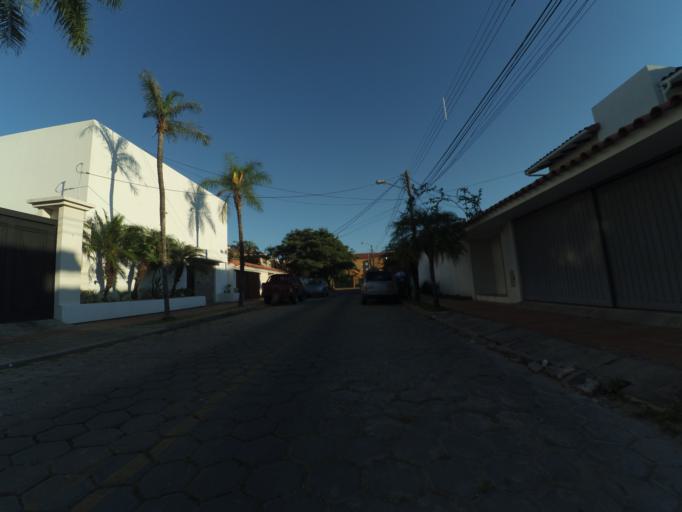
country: BO
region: Santa Cruz
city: Santa Cruz de la Sierra
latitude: -17.8040
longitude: -63.2052
